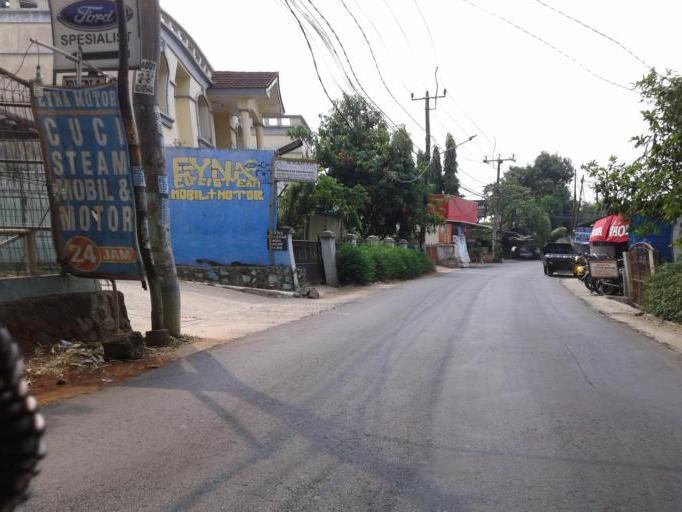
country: ID
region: Banten
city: South Tangerang
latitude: -6.2922
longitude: 106.7411
